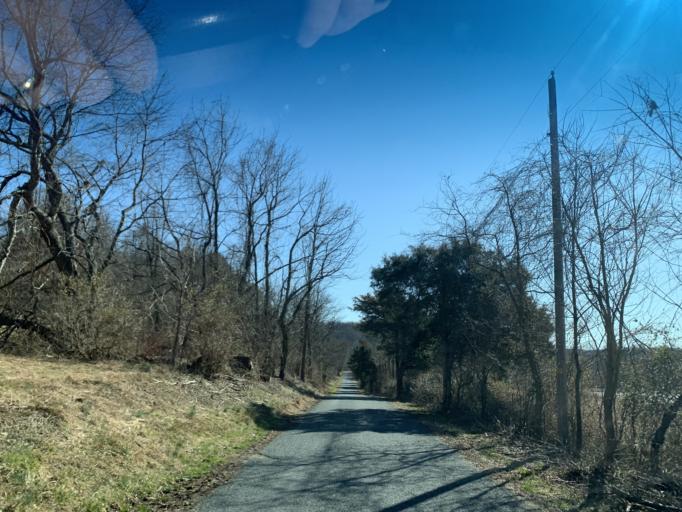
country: US
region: Maryland
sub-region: Harford County
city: Aberdeen
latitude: 39.6234
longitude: -76.2337
